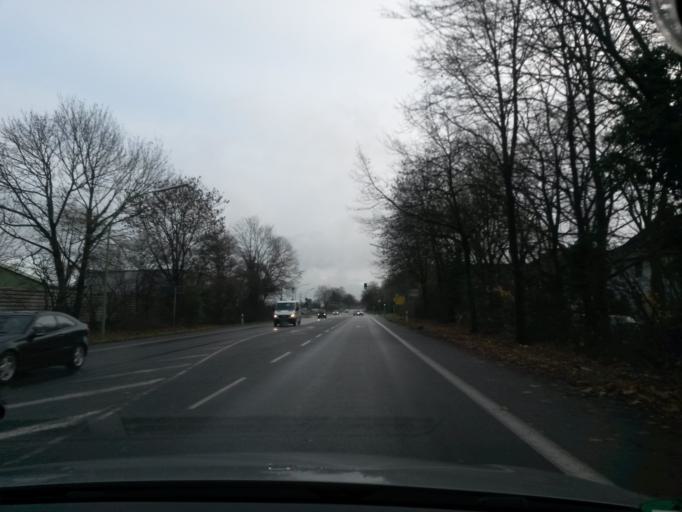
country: DE
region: North Rhine-Westphalia
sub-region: Regierungsbezirk Dusseldorf
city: Kamp-Lintfort
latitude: 51.5065
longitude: 6.5504
